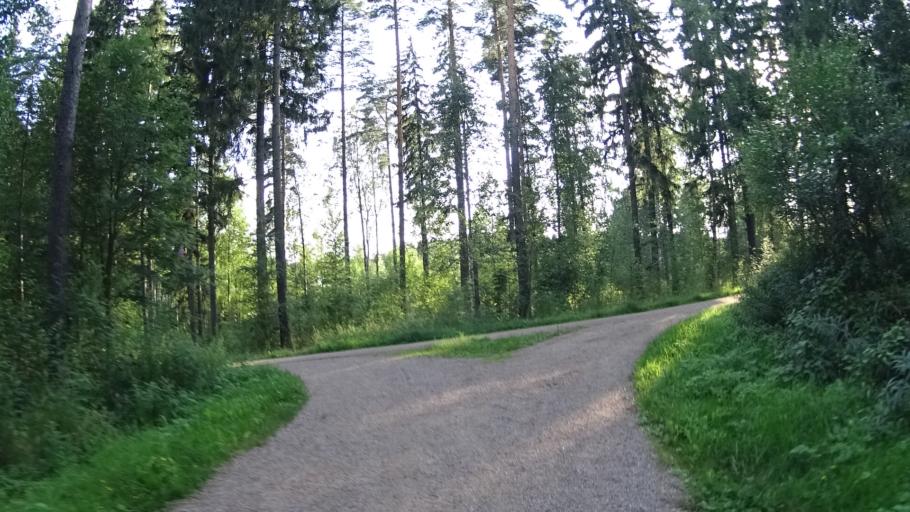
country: FI
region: Uusimaa
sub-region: Helsinki
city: Teekkarikylae
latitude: 60.2480
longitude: 24.8469
